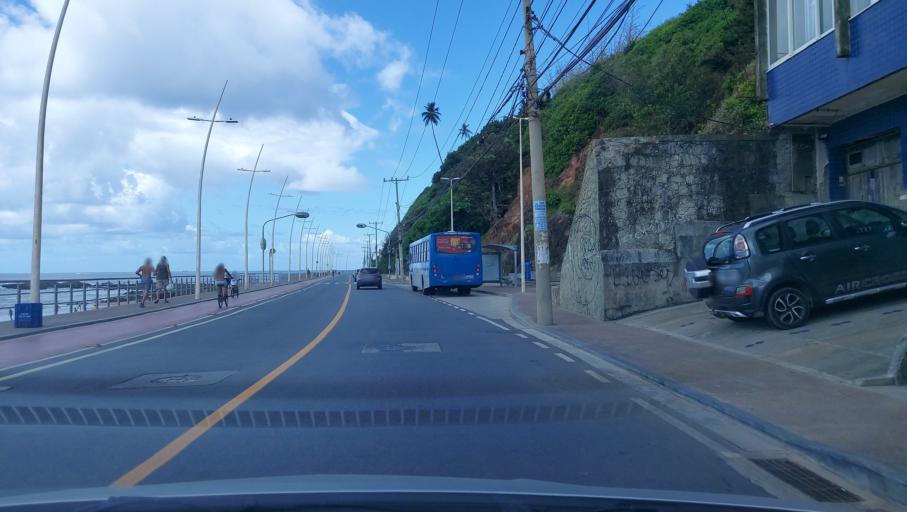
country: BR
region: Bahia
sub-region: Salvador
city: Salvador
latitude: -13.0104
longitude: -38.5031
